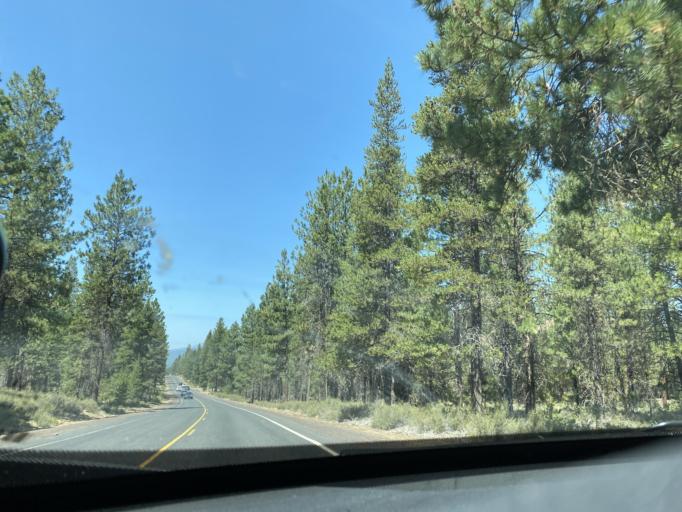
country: US
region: Oregon
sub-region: Deschutes County
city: Sunriver
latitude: 43.8905
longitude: -121.4025
